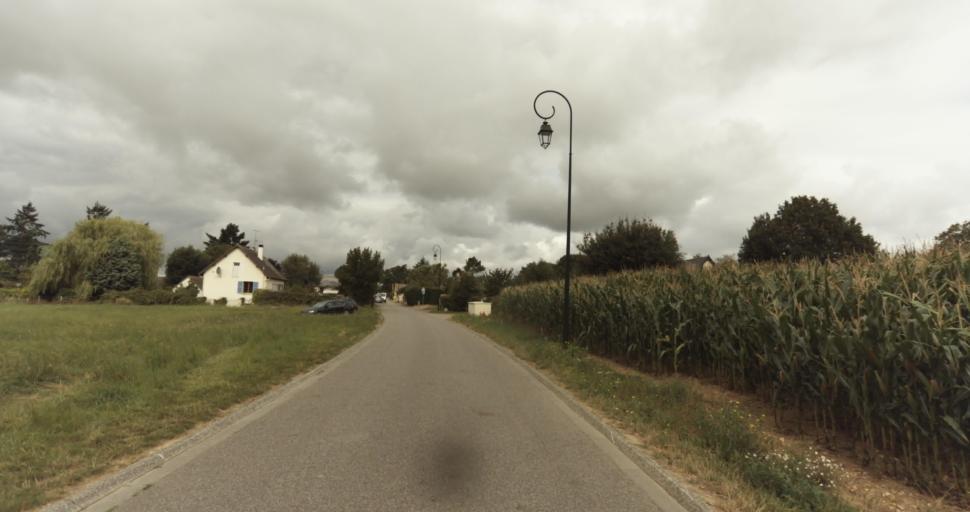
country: FR
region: Haute-Normandie
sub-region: Departement de l'Eure
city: Menilles
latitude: 48.9583
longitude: 1.2955
